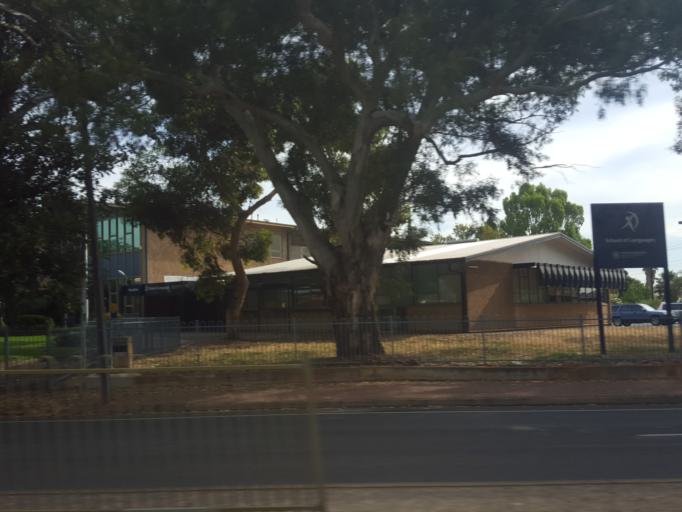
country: AU
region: South Australia
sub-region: Charles Sturt
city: Woodville
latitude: -34.8857
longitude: 138.5657
